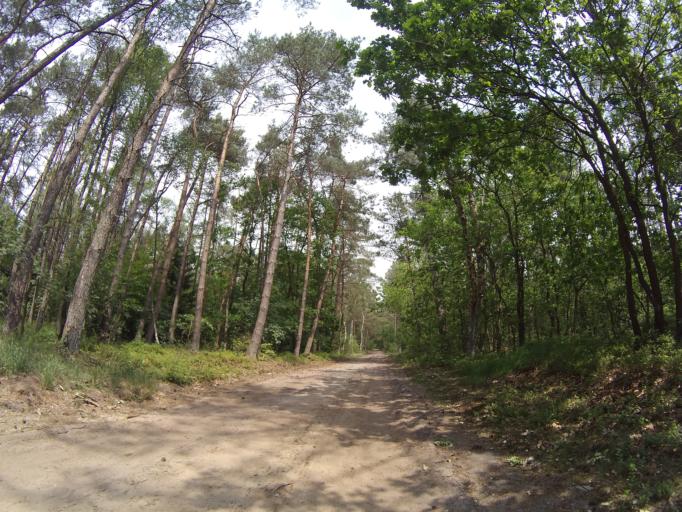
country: NL
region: Utrecht
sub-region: Gemeente Utrechtse Heuvelrug
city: Driebergen-Rijsenburg
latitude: 52.0955
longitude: 5.3164
